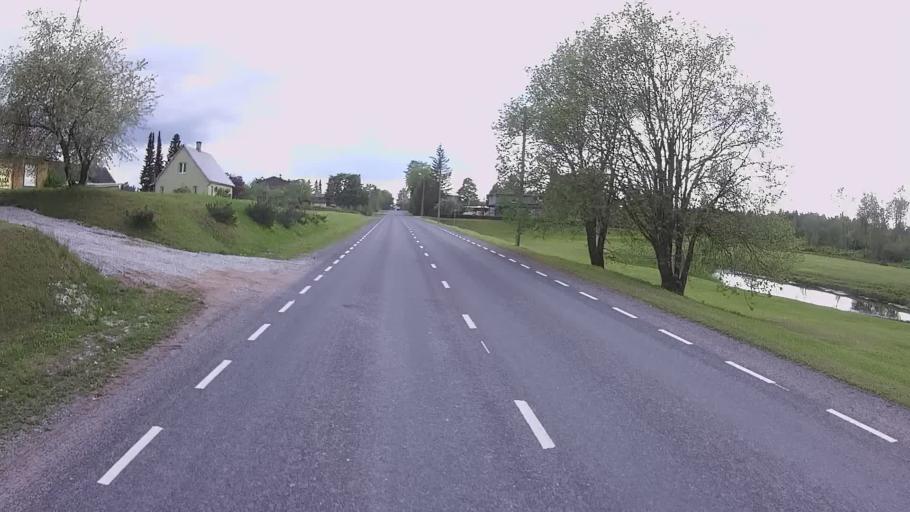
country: EE
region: Jogevamaa
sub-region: Mustvee linn
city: Mustvee
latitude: 58.9899
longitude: 26.8797
